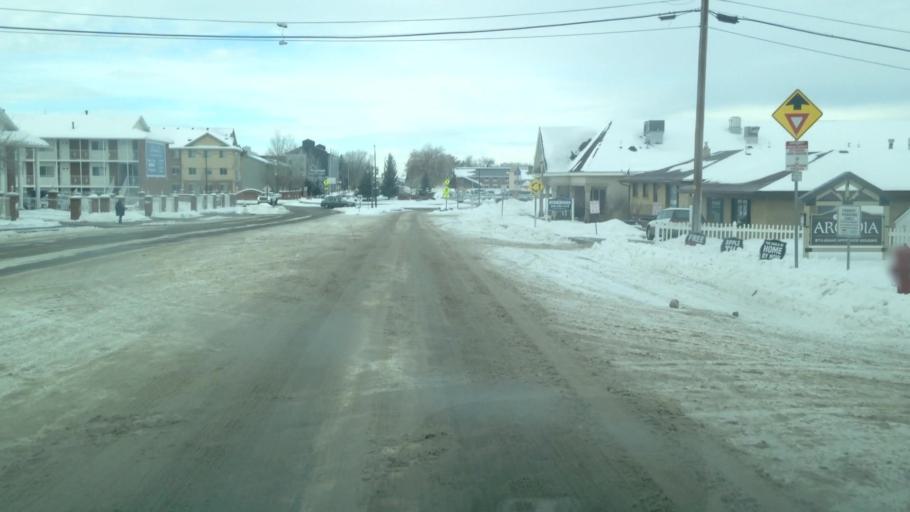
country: US
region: Idaho
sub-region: Madison County
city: Rexburg
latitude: 43.8178
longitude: -111.7877
